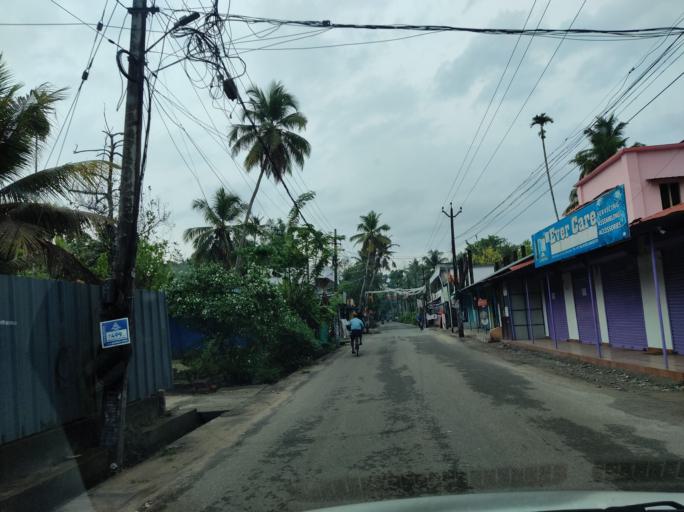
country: IN
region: Kerala
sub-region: Alappuzha
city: Kayankulam
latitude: 9.2179
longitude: 76.4613
